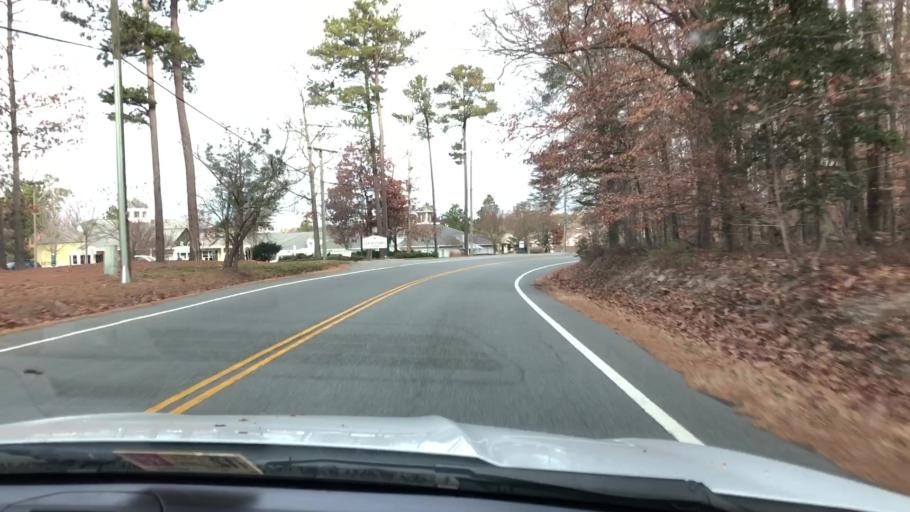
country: US
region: Virginia
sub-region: James City County
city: Williamsburg
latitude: 37.2645
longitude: -76.7407
